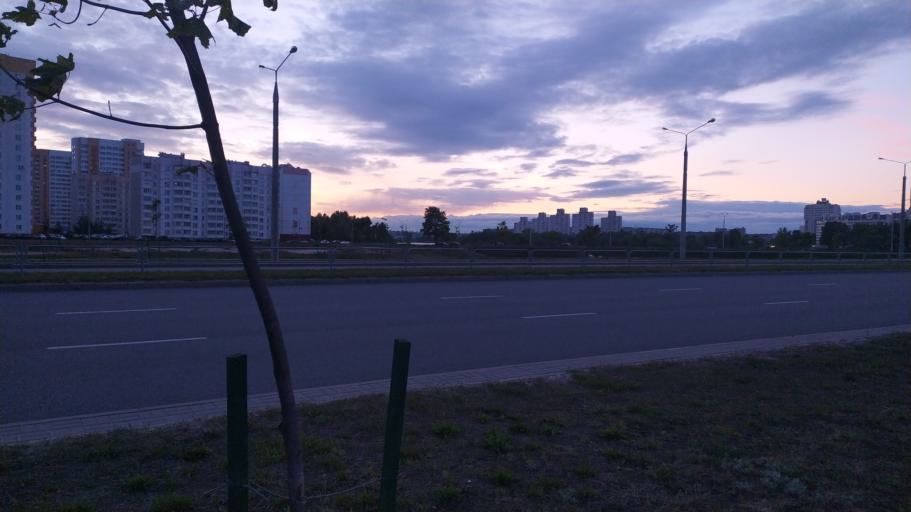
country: BY
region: Gomel
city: Gomel
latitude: 52.4580
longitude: 31.0356
